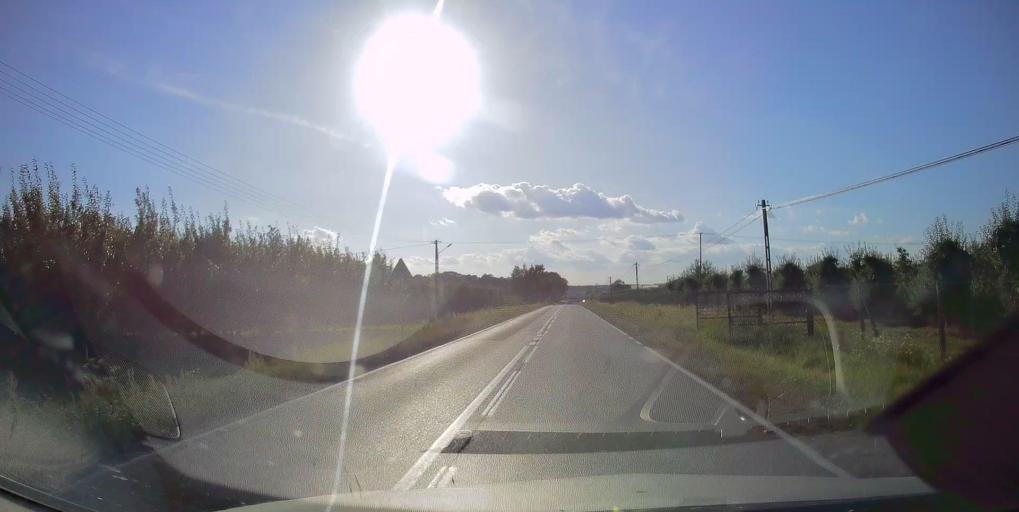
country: PL
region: Masovian Voivodeship
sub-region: Powiat grojecki
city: Bledow
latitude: 51.8132
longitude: 20.7481
